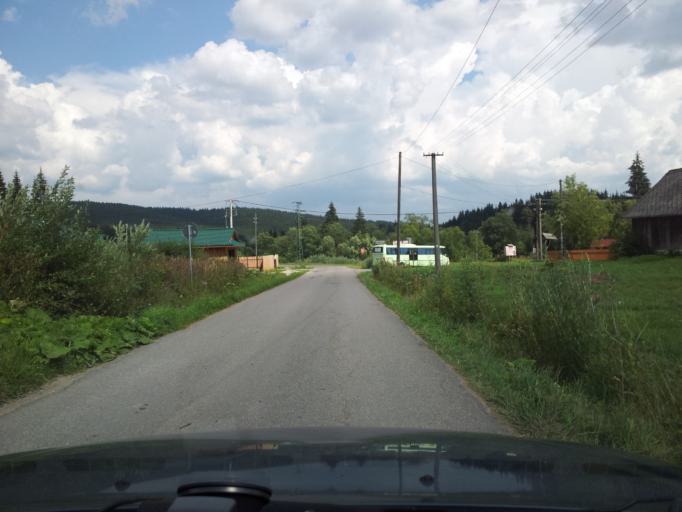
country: SK
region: Zilinsky
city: Oravska Lesna
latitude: 49.3819
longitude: 19.2221
